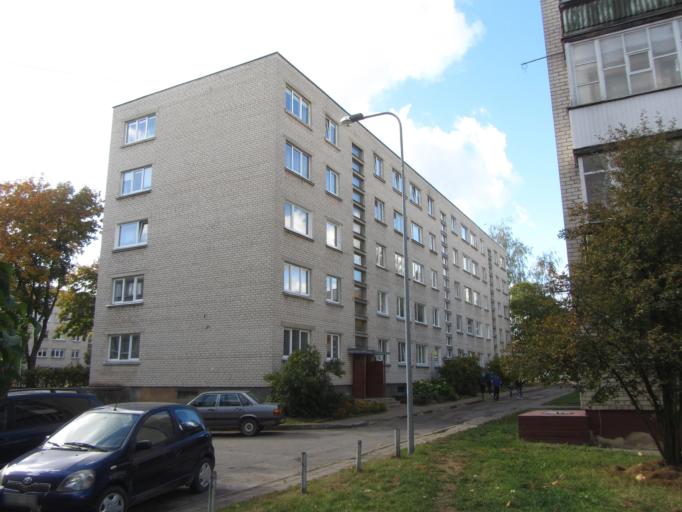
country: LT
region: Utenos apskritis
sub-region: Utena
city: Utena
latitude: 55.5039
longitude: 25.6171
